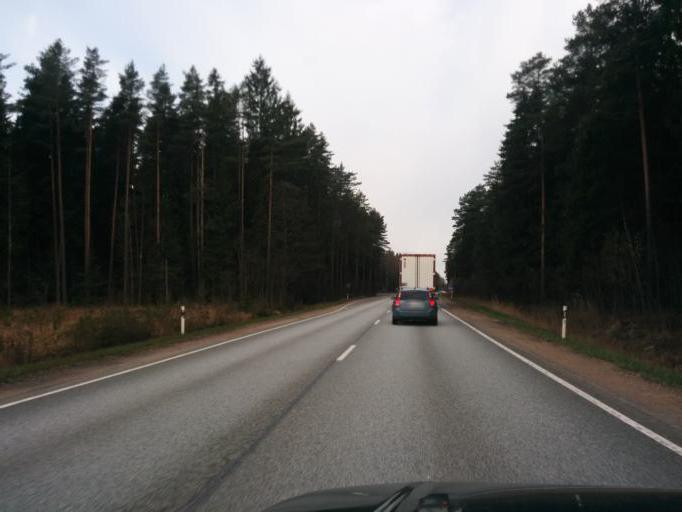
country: LV
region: Kekava
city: Balozi
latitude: 56.8263
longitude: 24.0615
